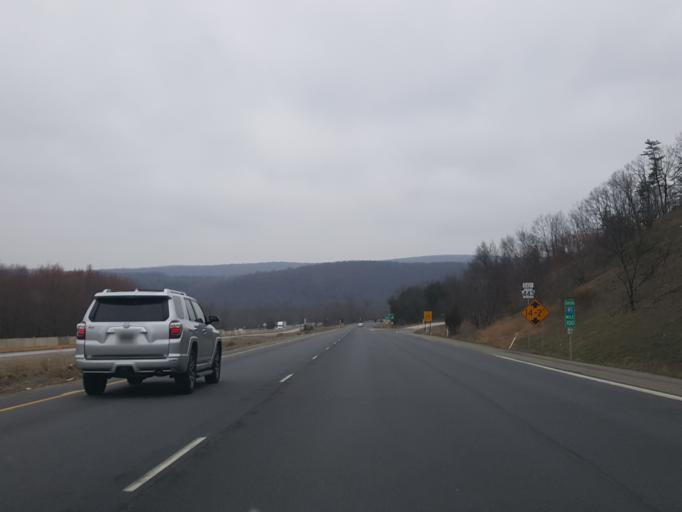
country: US
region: Pennsylvania
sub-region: Schuylkill County
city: Pine Grove
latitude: 40.5400
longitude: -76.4297
